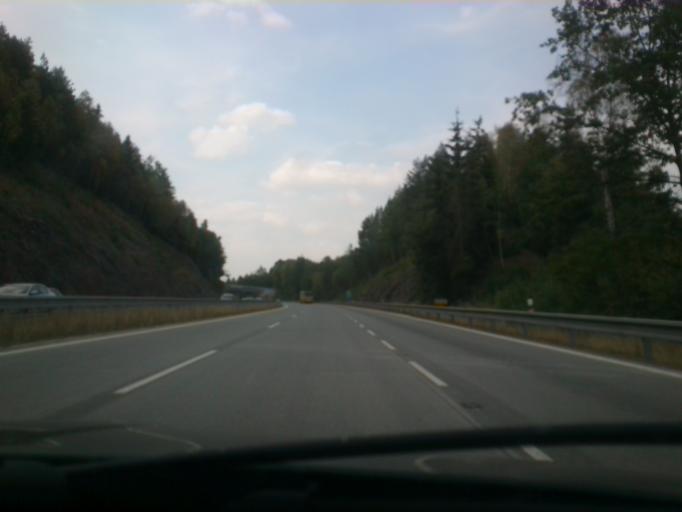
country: CZ
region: Central Bohemia
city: Divisov
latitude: 49.7915
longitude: 14.9254
